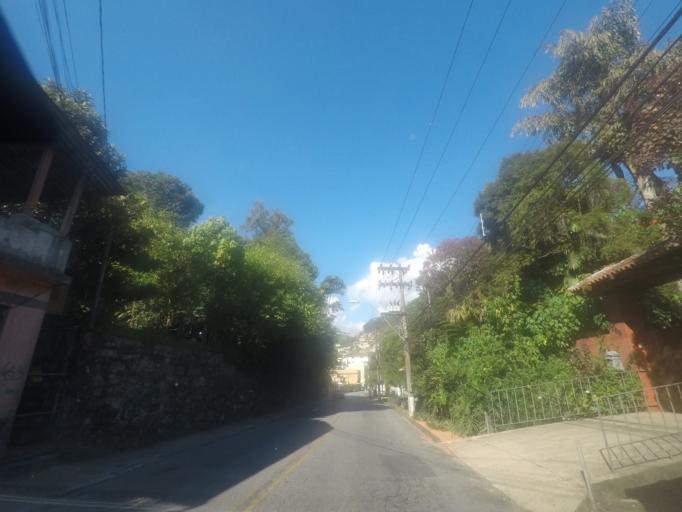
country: BR
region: Rio de Janeiro
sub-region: Petropolis
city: Petropolis
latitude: -22.5243
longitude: -43.1856
